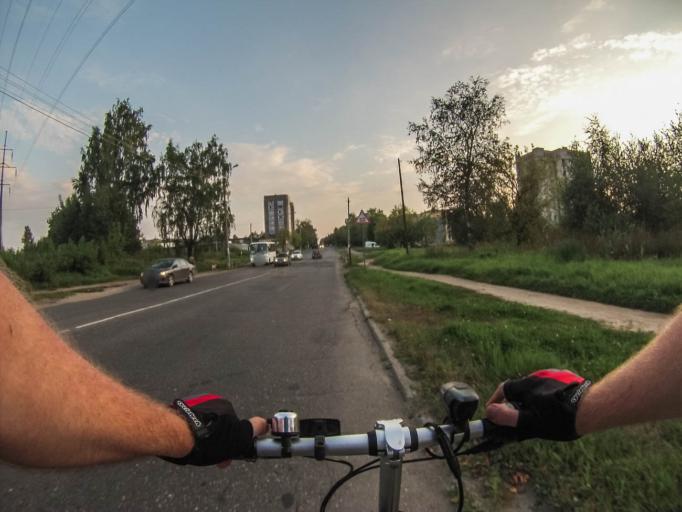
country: RU
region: Kostroma
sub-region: Kostromskoy Rayon
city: Kostroma
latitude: 57.7942
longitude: 40.9482
